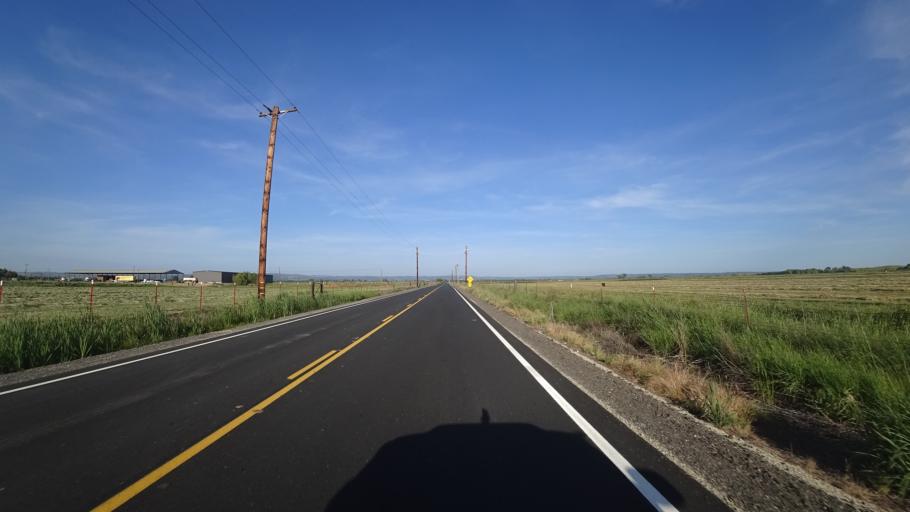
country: US
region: California
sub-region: Placer County
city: Lincoln
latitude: 38.9264
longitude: -121.3186
